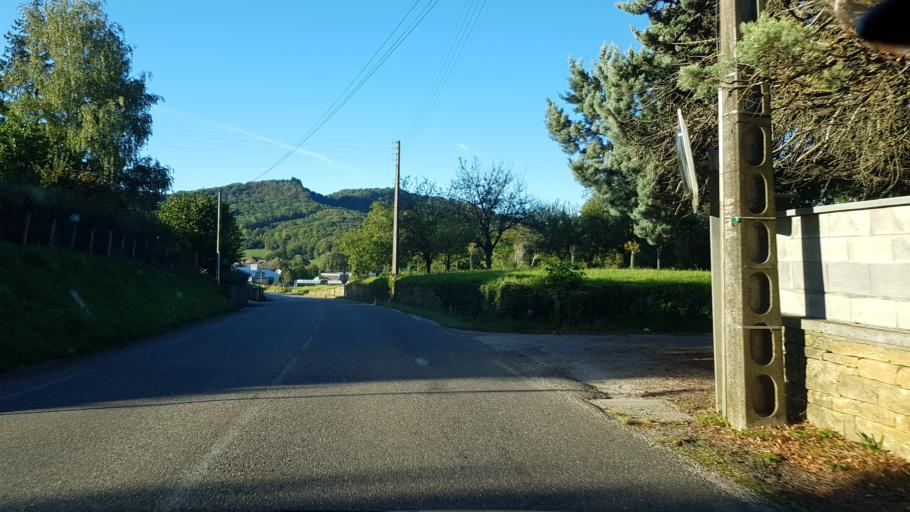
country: FR
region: Franche-Comte
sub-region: Departement du Jura
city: Lons-le-Saunier
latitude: 46.6555
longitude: 5.5388
